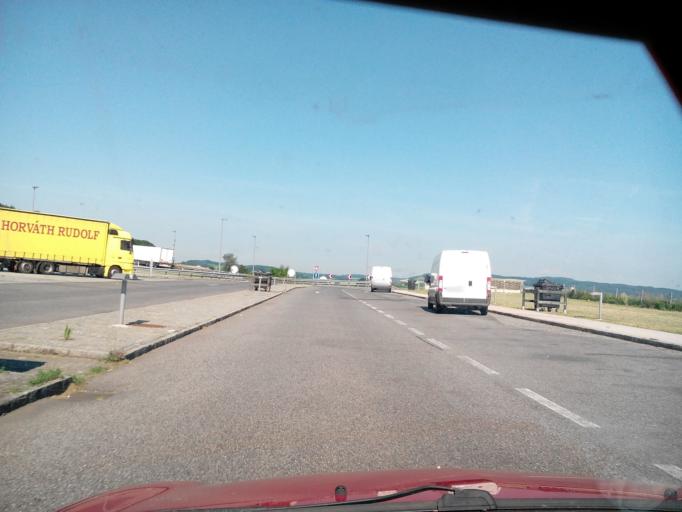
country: AT
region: Lower Austria
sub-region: Politischer Bezirk Sankt Polten
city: Kirchstetten
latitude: 48.1859
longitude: 15.7964
